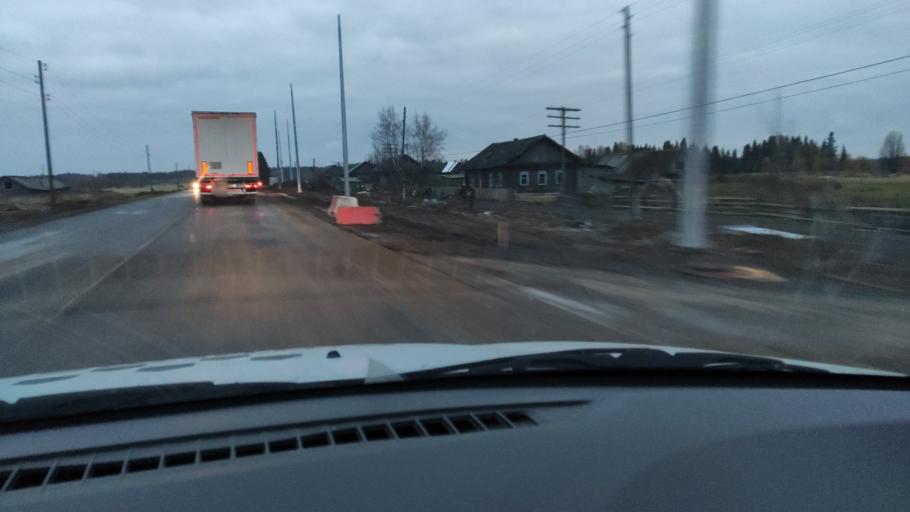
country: RU
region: Kirov
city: Kostino
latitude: 58.8311
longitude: 53.3076
